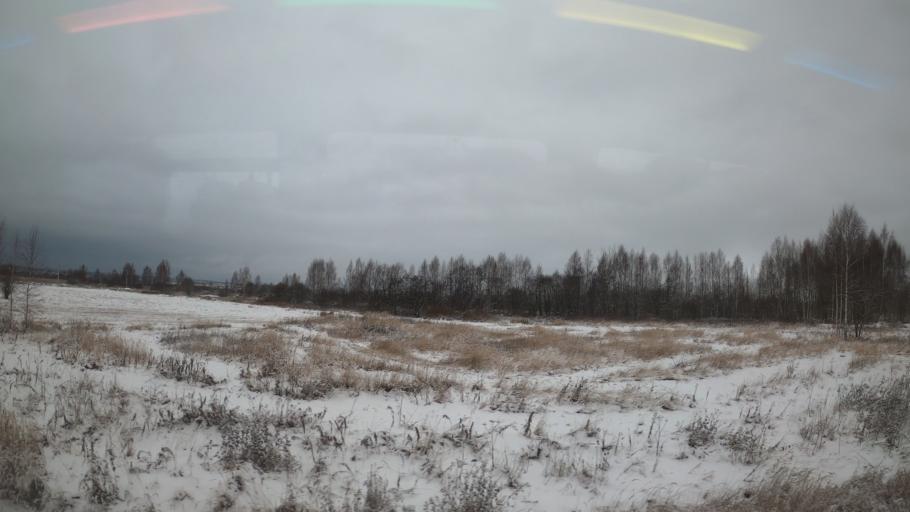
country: RU
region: Jaroslavl
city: Pereslavl'-Zalesskiy
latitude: 56.7232
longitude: 38.9055
